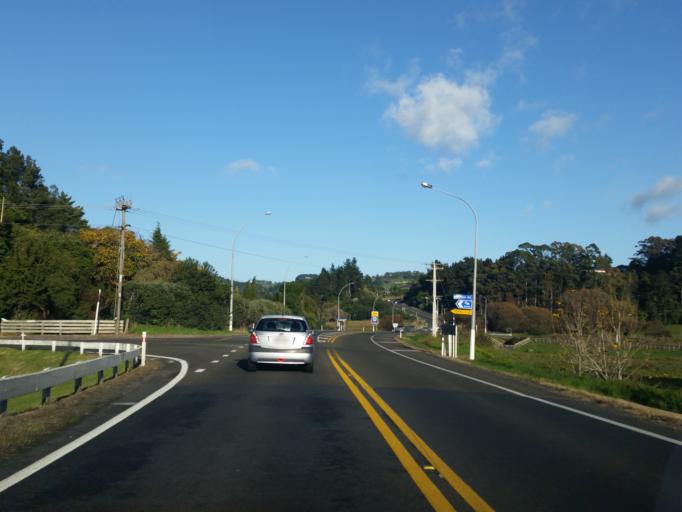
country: NZ
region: Bay of Plenty
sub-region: Tauranga City
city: Tauranga
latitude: -37.6992
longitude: 176.0939
